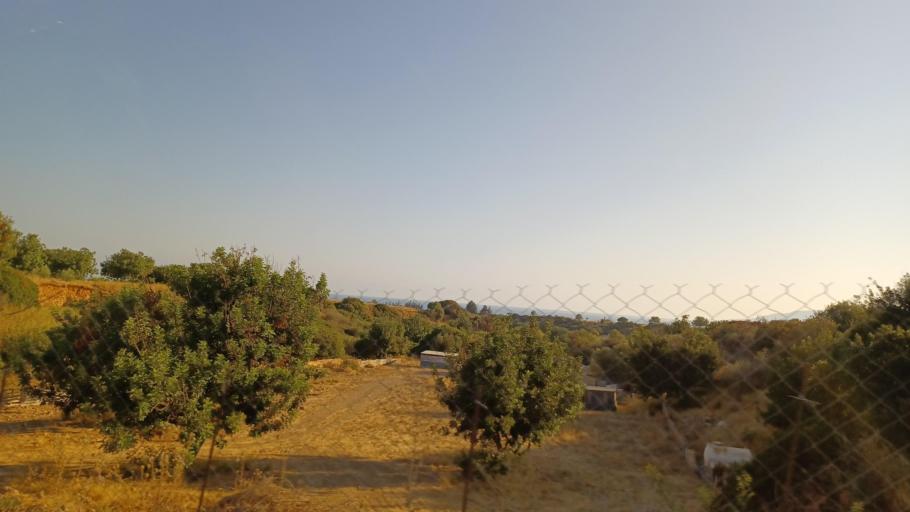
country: CY
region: Pafos
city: Polis
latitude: 35.0228
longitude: 32.3935
